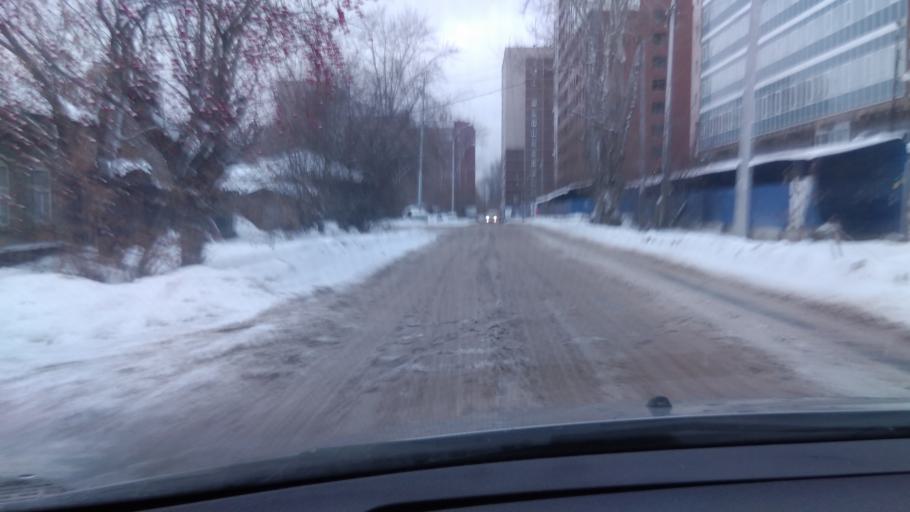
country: RU
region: Sverdlovsk
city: Yekaterinburg
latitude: 56.8052
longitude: 60.5964
